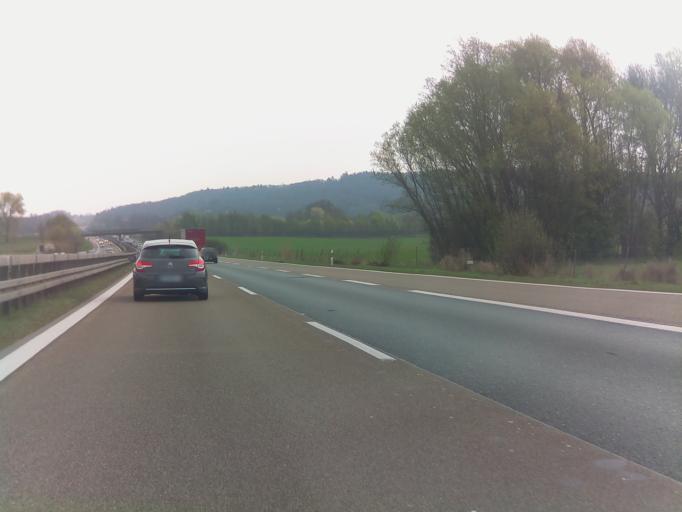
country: DE
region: Baden-Wuerttemberg
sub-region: Regierungsbezirk Stuttgart
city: Satteldorf
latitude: 49.1908
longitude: 10.1102
